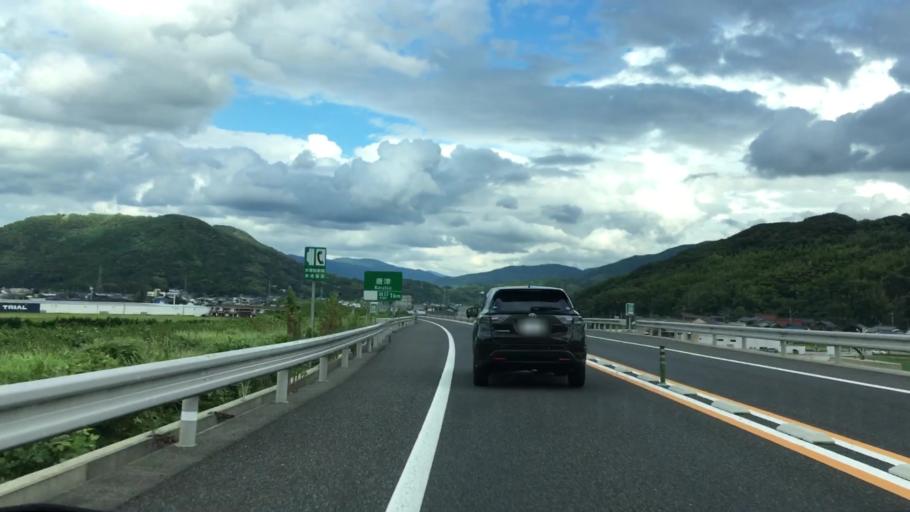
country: JP
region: Saga Prefecture
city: Karatsu
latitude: 33.4122
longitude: 129.9889
